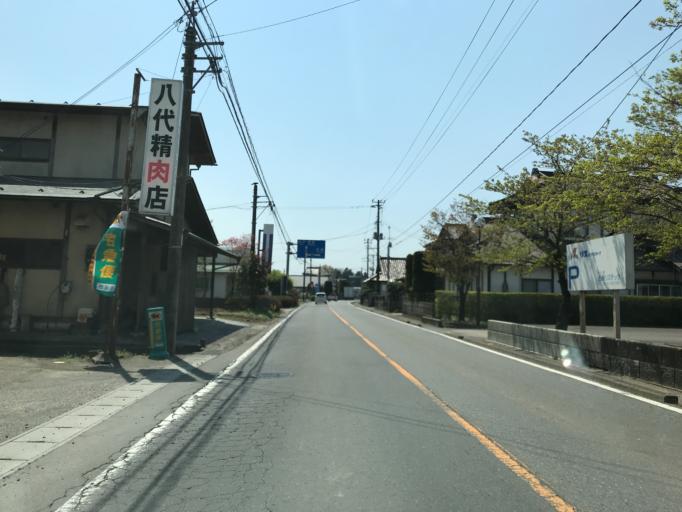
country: JP
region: Fukushima
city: Ishikawa
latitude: 37.1314
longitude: 140.3500
